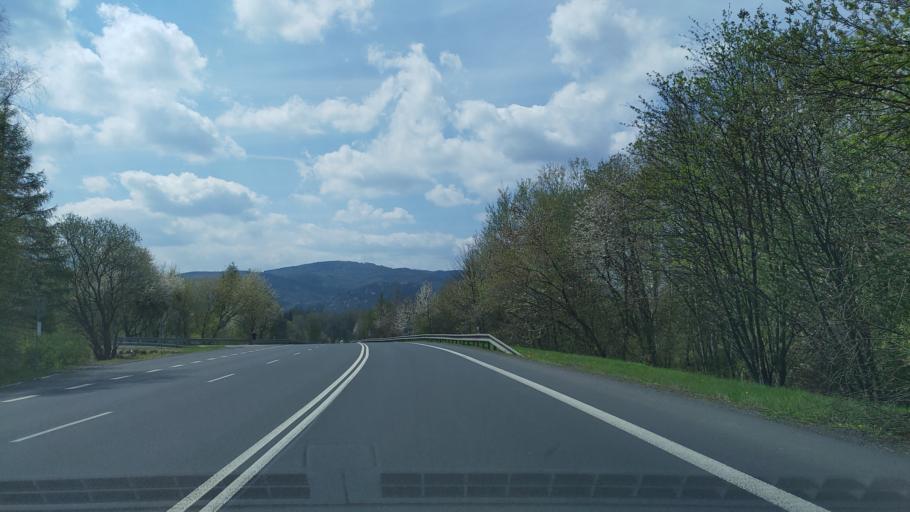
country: CZ
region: Ustecky
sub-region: Okres Chomutov
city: Perstejn
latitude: 50.3836
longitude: 13.1455
